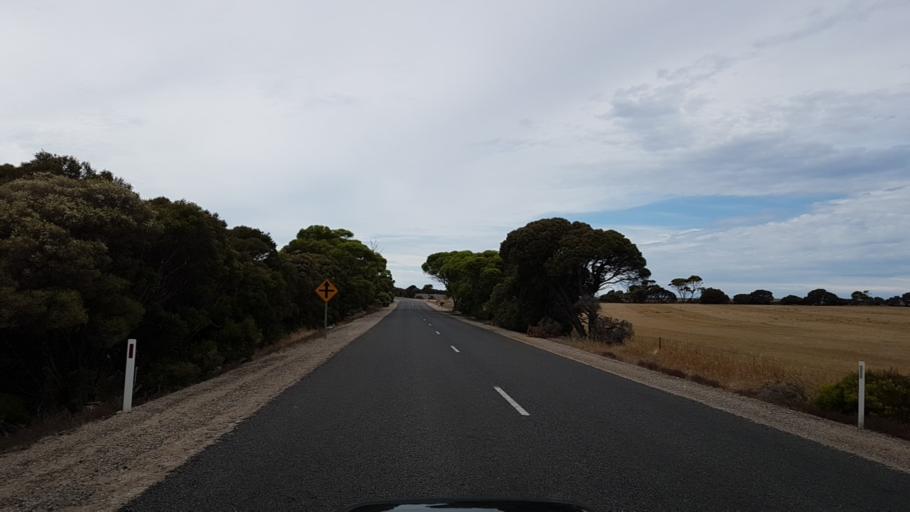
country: AU
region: South Australia
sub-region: Yorke Peninsula
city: Honiton
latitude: -34.9679
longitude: 137.1096
